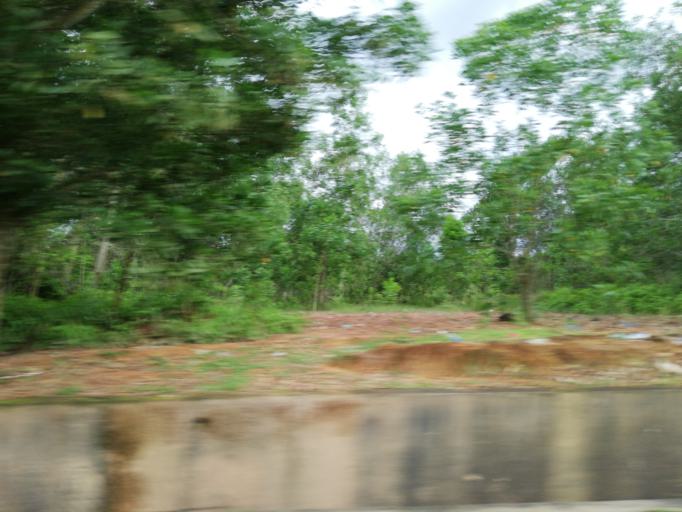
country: MY
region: Penang
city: Tasek Glugor
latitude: 5.4964
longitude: 100.6247
